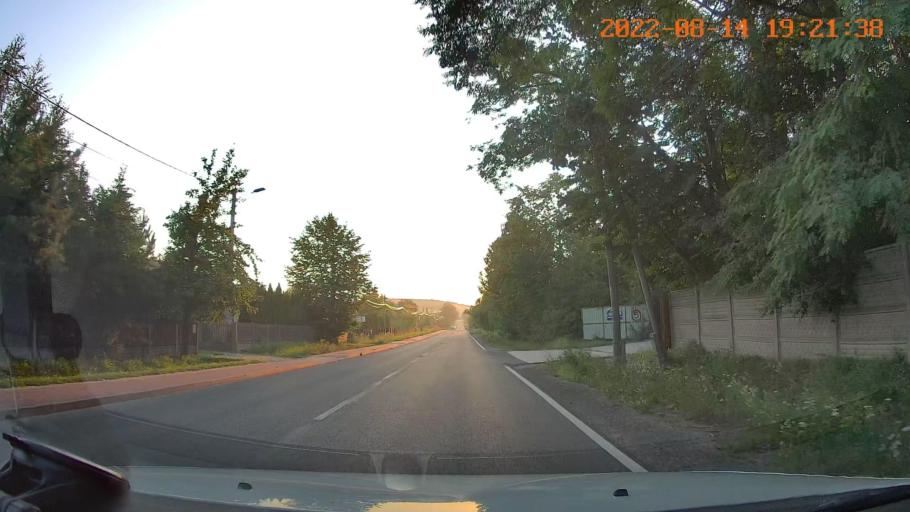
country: PL
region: Swietokrzyskie
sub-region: Powiat kielecki
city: Piekoszow
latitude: 50.8591
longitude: 20.4924
